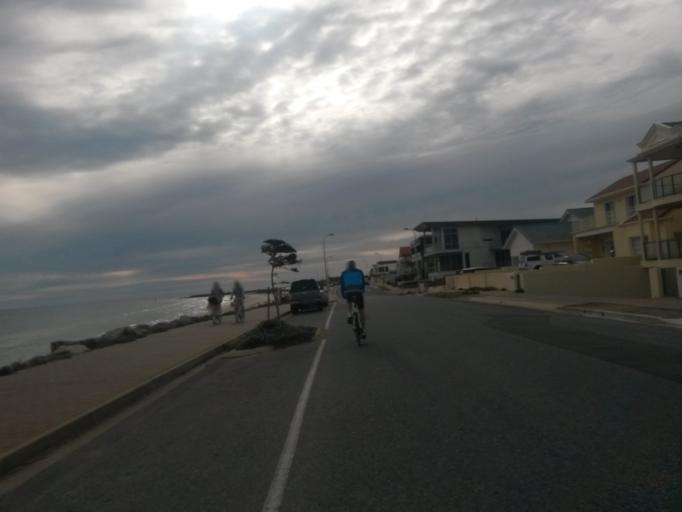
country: AU
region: South Australia
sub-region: Adelaide
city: Glenelg
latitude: -34.9676
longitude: 138.5100
